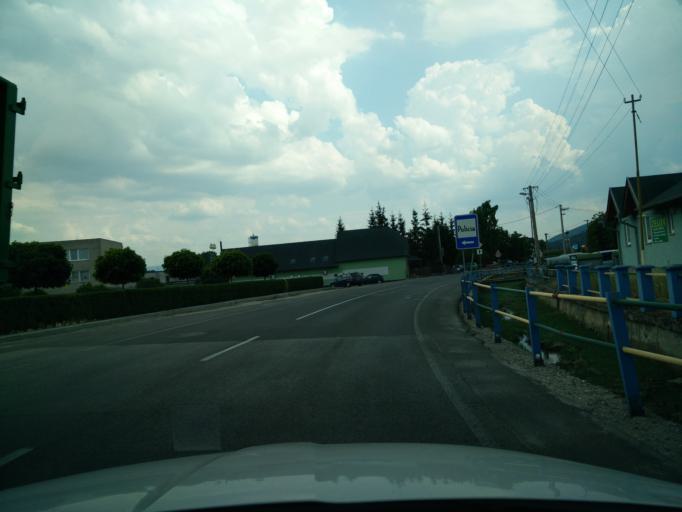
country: SK
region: Nitriansky
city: Novaky
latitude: 48.7979
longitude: 18.4776
